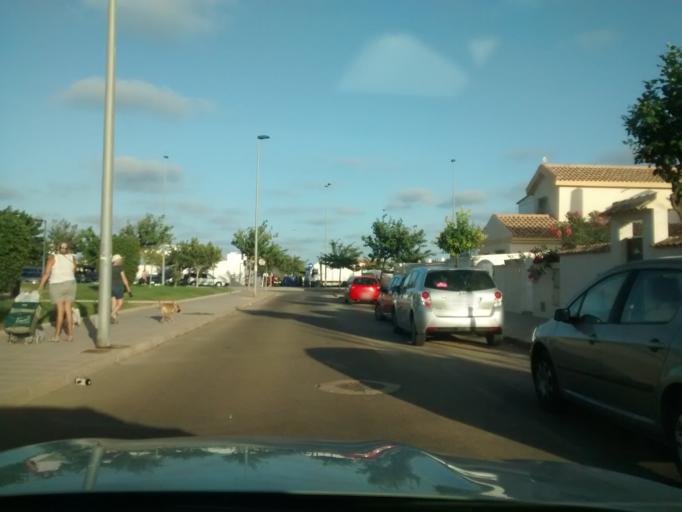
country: ES
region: Valencia
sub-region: Provincia de Alicante
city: Pilar de la Horadada
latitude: 37.8694
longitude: -0.7686
